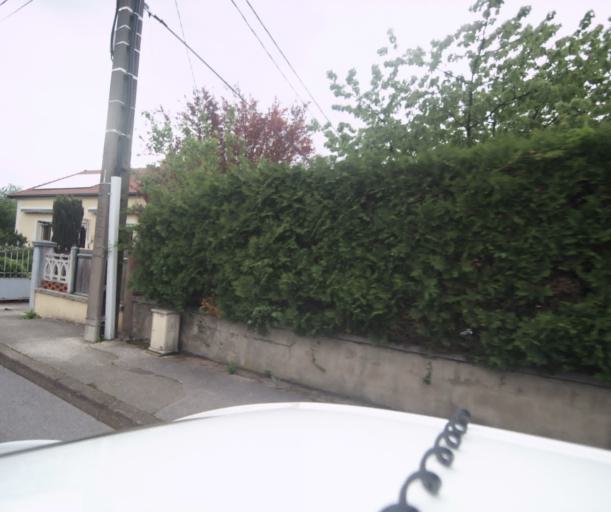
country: FR
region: Franche-Comte
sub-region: Departement du Doubs
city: Beure
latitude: 47.2298
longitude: 5.9847
